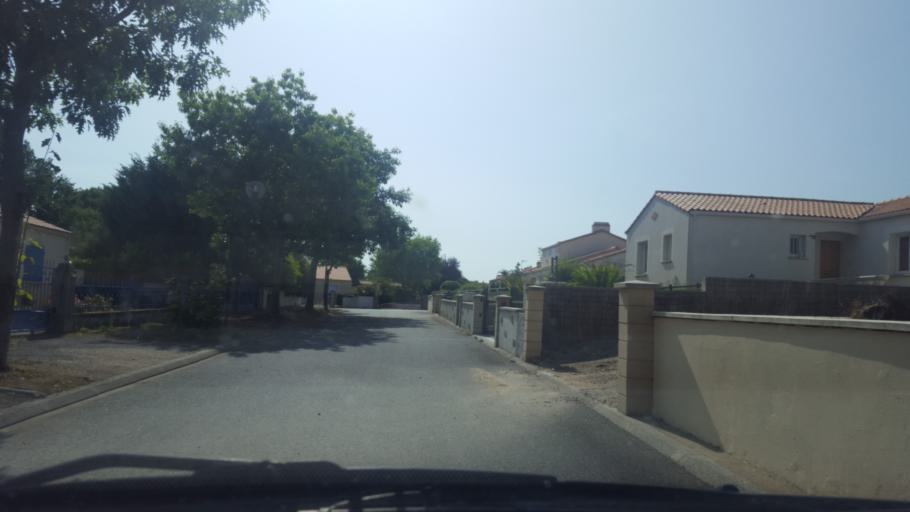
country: FR
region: Pays de la Loire
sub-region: Departement de la Loire-Atlantique
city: Saint-Philbert-de-Grand-Lieu
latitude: 47.0353
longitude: -1.6494
